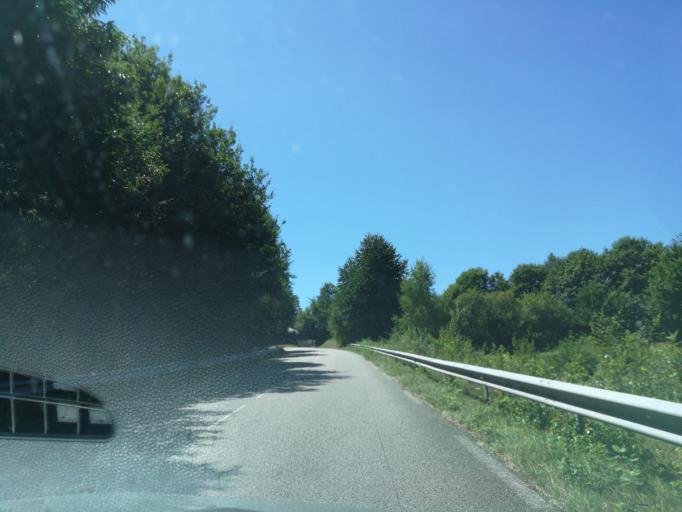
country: FR
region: Limousin
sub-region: Departement de la Correze
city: Argentat
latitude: 45.0473
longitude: 1.9490
